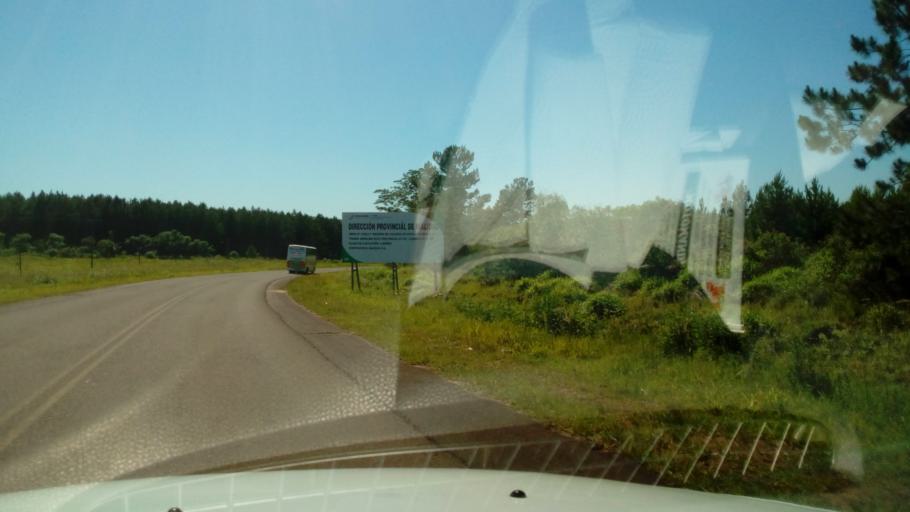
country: AR
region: Misiones
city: Santa Ana
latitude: -27.4150
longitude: -55.5254
